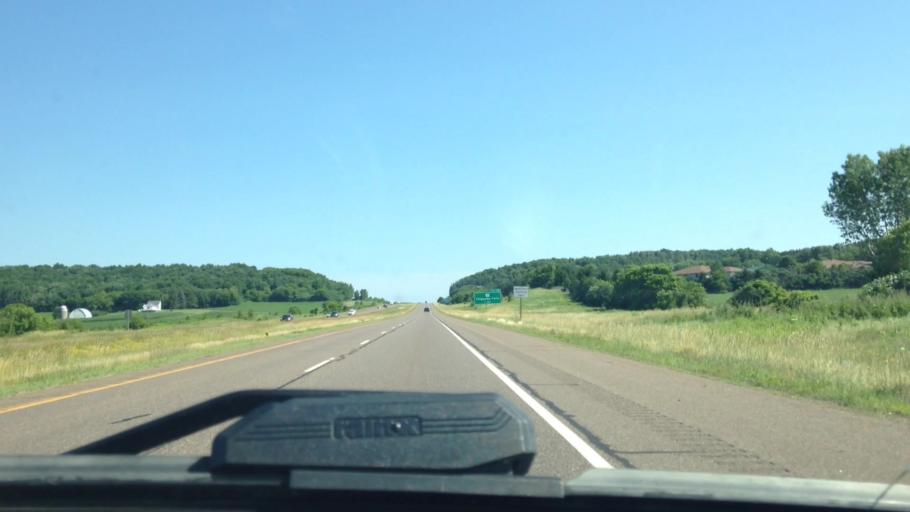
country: US
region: Wisconsin
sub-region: Chippewa County
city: Chippewa Falls
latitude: 44.9449
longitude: -91.4268
